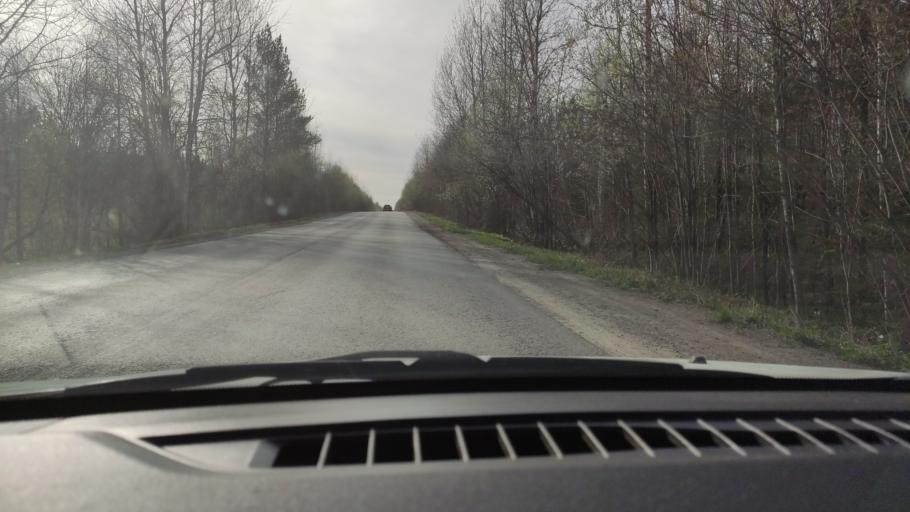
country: RU
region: Perm
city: Ferma
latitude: 57.9387
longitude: 56.4541
